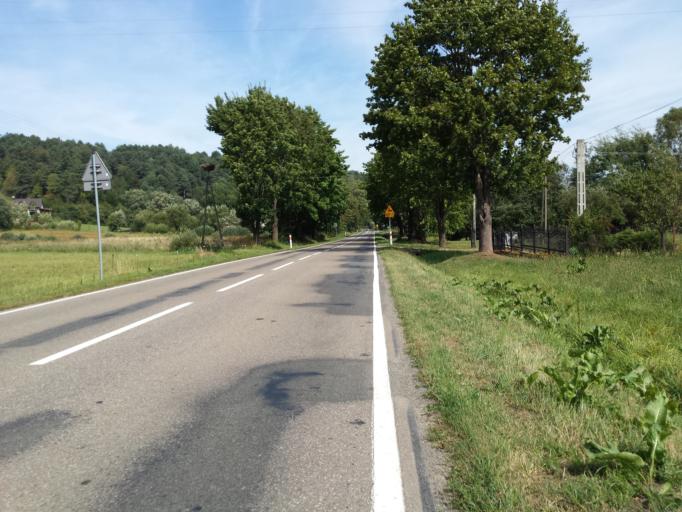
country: PL
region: Subcarpathian Voivodeship
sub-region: Powiat leski
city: Baligrod
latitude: 49.3760
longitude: 22.2761
